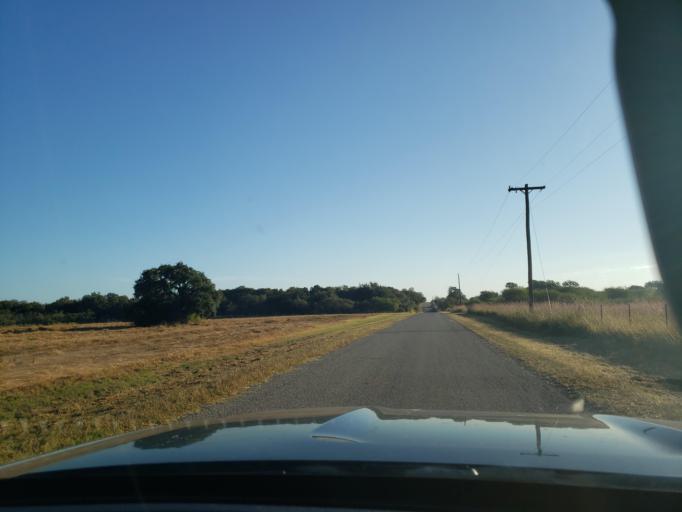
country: US
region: Texas
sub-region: Bee County
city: Beeville
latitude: 28.4230
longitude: -97.7068
